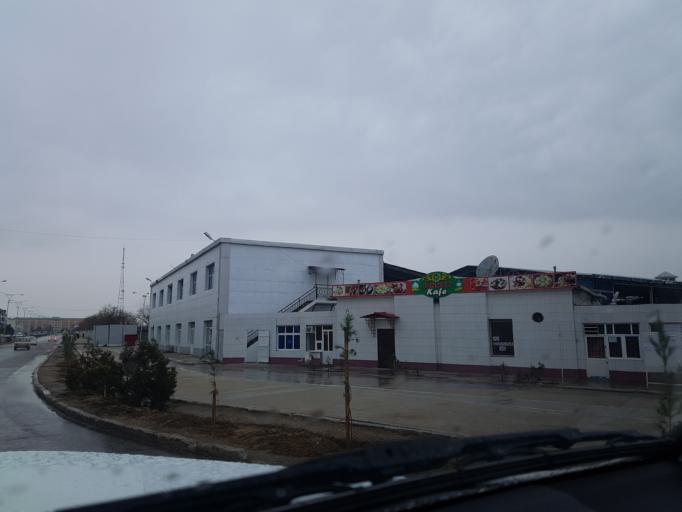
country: TM
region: Balkan
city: Balkanabat
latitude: 39.5218
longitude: 54.3566
